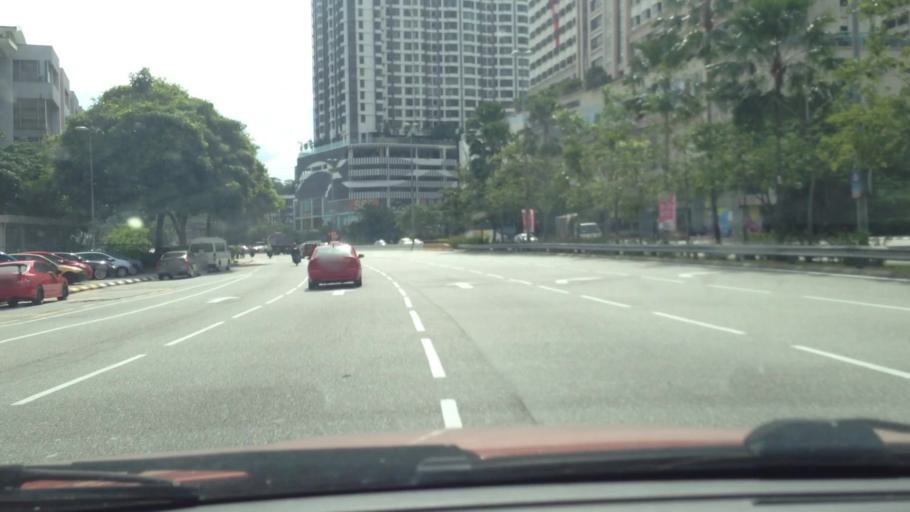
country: MY
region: Kuala Lumpur
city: Kuala Lumpur
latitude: 3.0845
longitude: 101.6721
